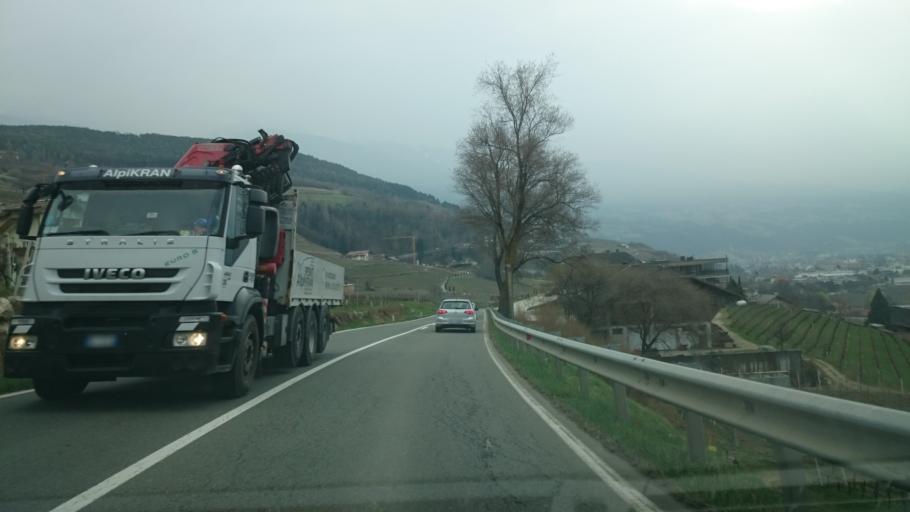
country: IT
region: Trentino-Alto Adige
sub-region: Bolzano
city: Varna
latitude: 46.7463
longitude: 11.6498
